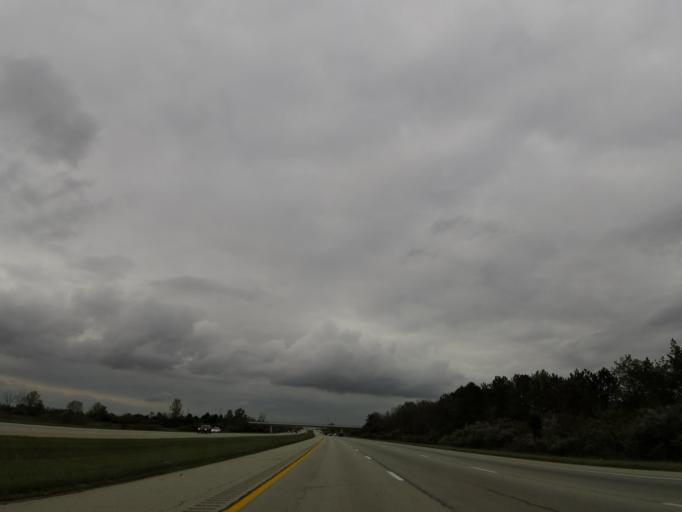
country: US
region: Ohio
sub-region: Fayette County
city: Jeffersonville
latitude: 39.6029
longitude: -83.6376
